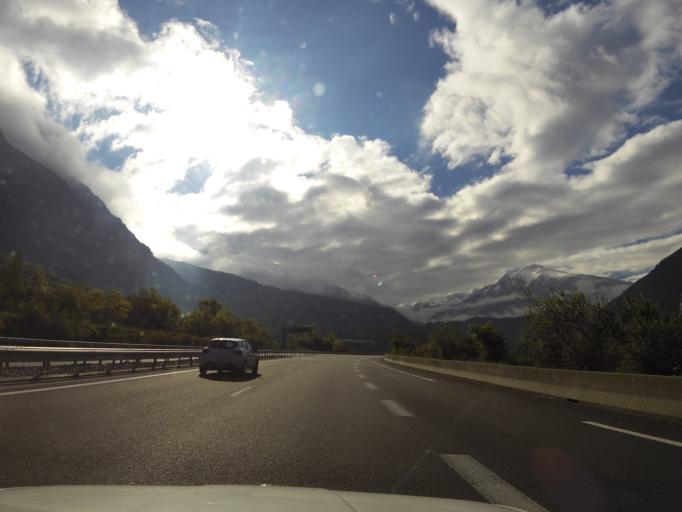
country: FR
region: Rhone-Alpes
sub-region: Departement de la Savoie
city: Saint-Michel-de-Maurienne
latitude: 45.2450
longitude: 6.4284
